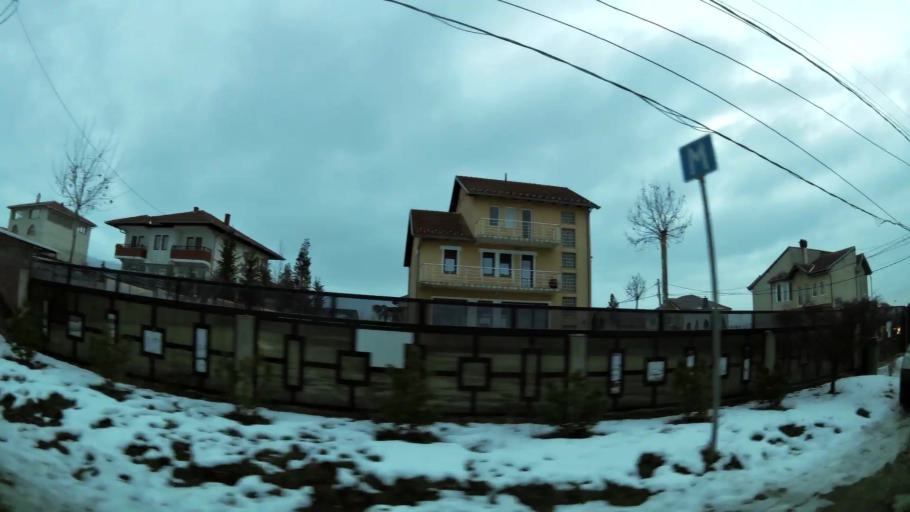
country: XK
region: Pristina
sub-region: Komuna e Prishtines
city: Pristina
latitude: 42.6294
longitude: 21.1641
